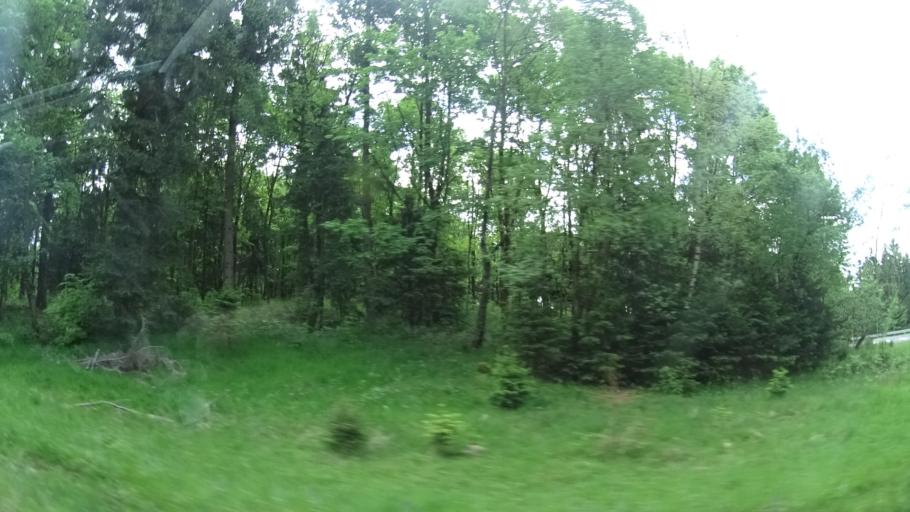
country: DE
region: Thuringia
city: Suhl
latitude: 50.6174
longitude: 10.7301
